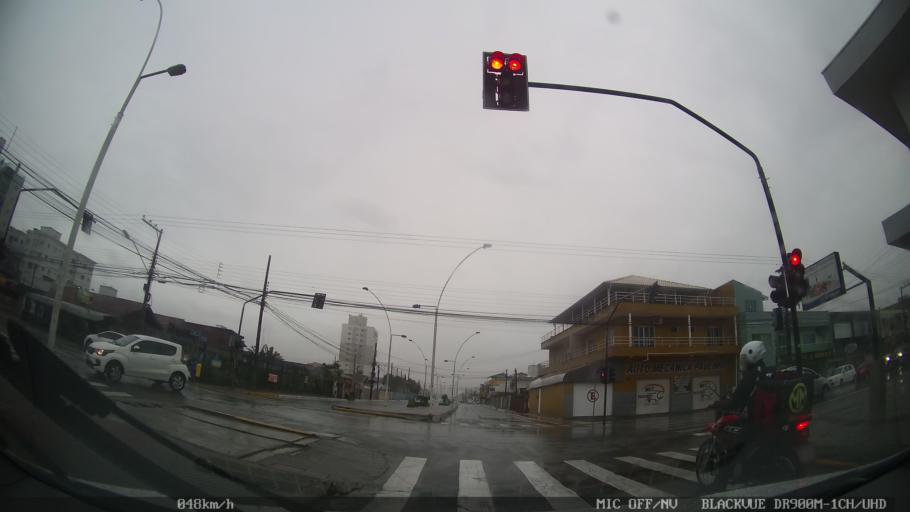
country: BR
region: Santa Catarina
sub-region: Itajai
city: Itajai
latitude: -26.9190
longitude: -48.6772
